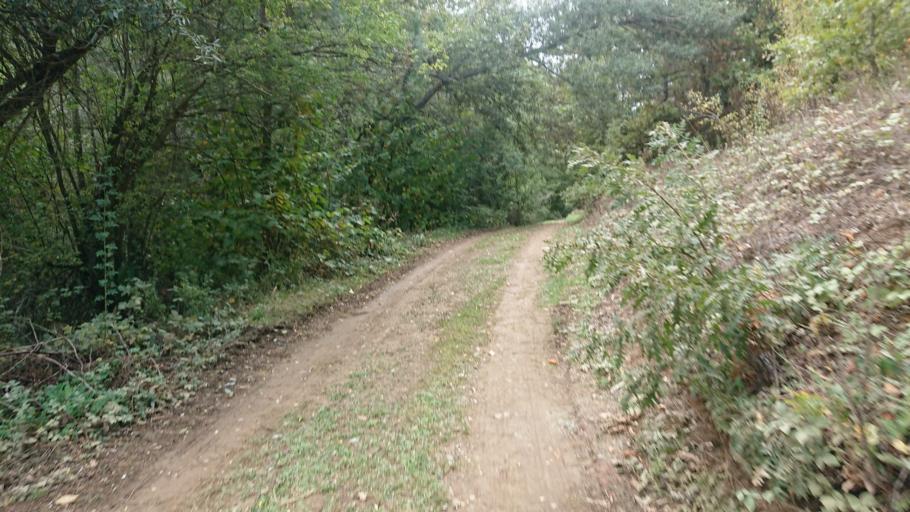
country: TR
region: Bilecik
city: Pazaryeri
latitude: 40.0179
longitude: 29.7887
